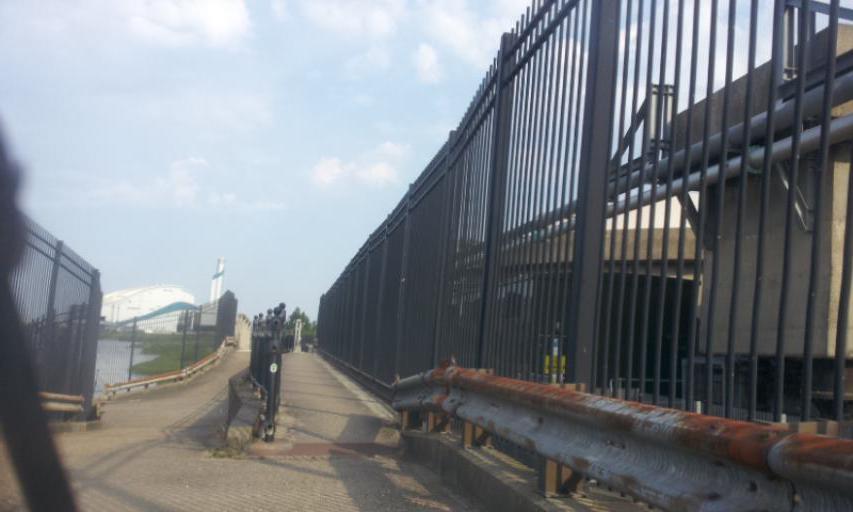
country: GB
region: England
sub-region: Greater London
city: Belvedere
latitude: 51.5079
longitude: 0.1434
